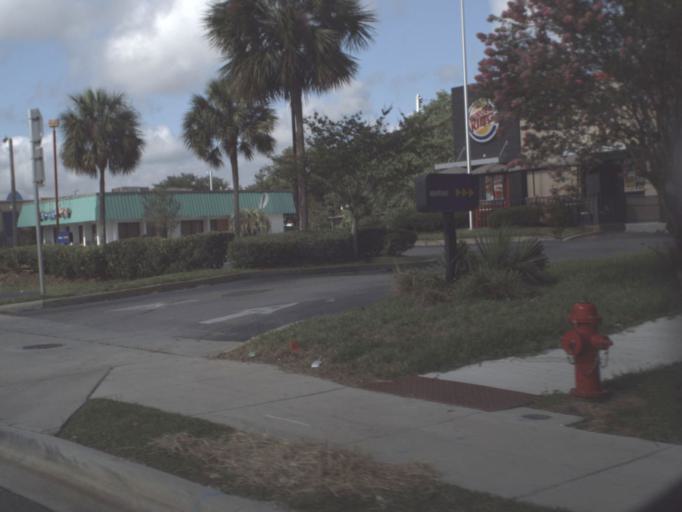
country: US
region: Florida
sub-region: Lake County
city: Leesburg
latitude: 28.8269
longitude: -81.8875
